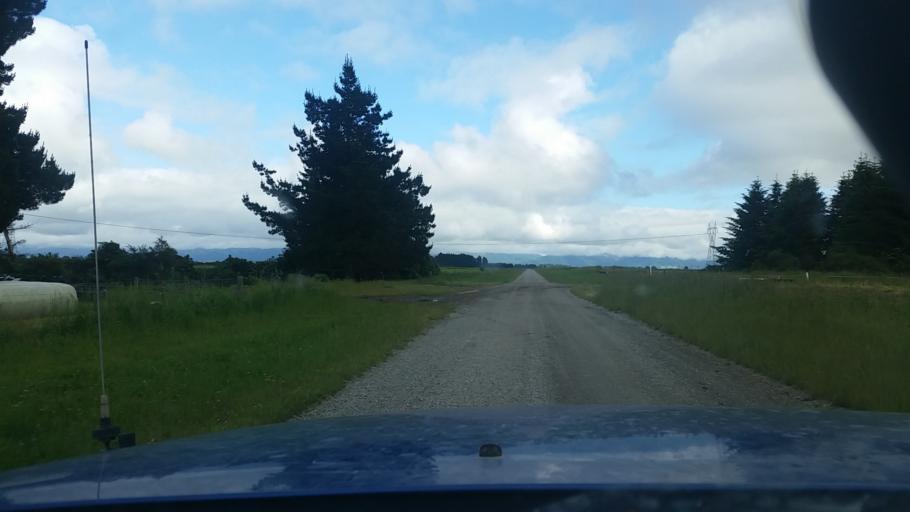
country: NZ
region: Canterbury
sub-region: Timaru District
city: Pleasant Point
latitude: -44.0161
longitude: 171.3648
